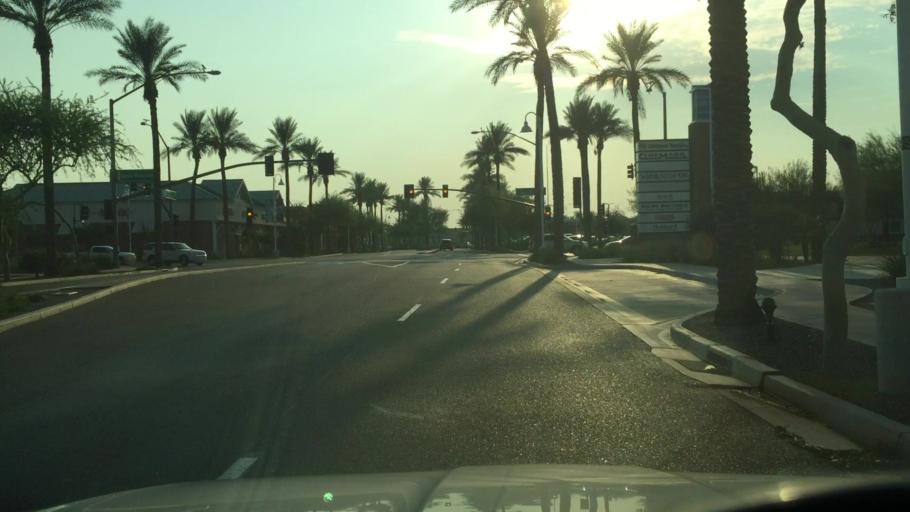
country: US
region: Arizona
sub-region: Maricopa County
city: Mesa
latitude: 33.4343
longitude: -111.8664
